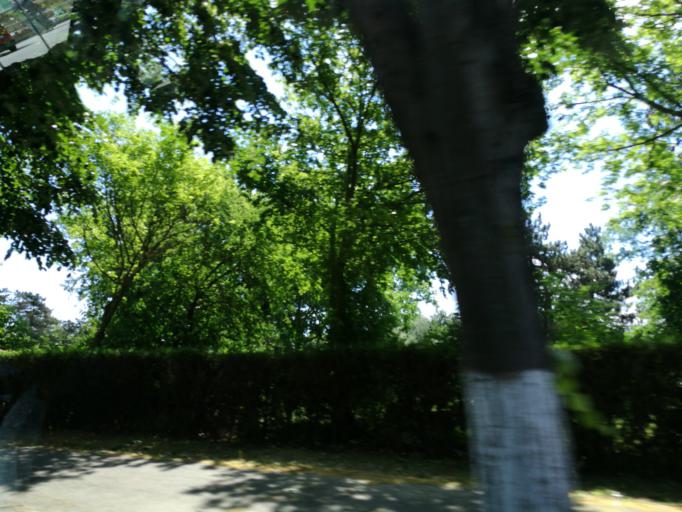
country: RO
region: Constanta
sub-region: Oras Eforie
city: Eforie Nord
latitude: 44.0591
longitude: 28.6345
